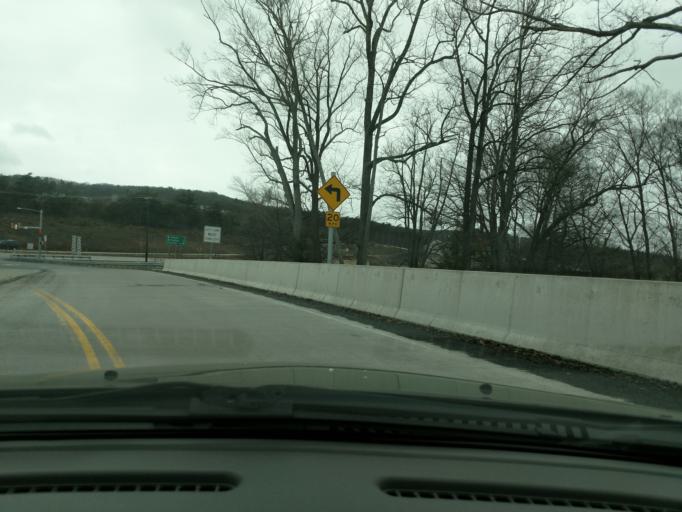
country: US
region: Pennsylvania
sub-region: Schuylkill County
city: Orwigsburg
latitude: 40.6202
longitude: -76.0570
